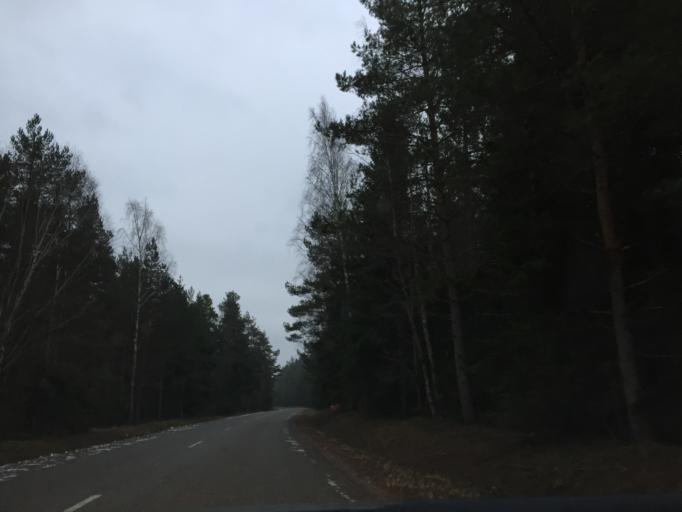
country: EE
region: Saare
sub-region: Kuressaare linn
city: Kuressaare
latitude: 58.6049
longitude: 22.6021
